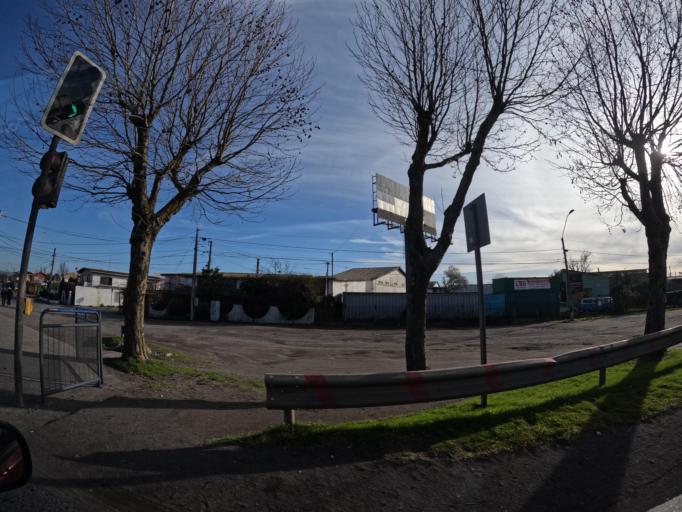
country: CL
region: Biobio
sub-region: Provincia de Concepcion
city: Concepcion
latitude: -36.7745
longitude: -73.0808
